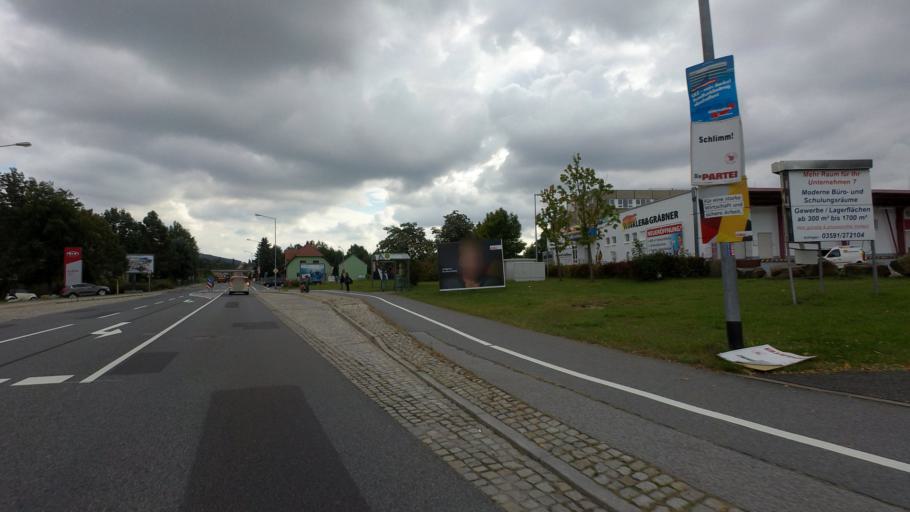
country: DE
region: Saxony
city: Bautzen
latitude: 51.1641
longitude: 14.4280
